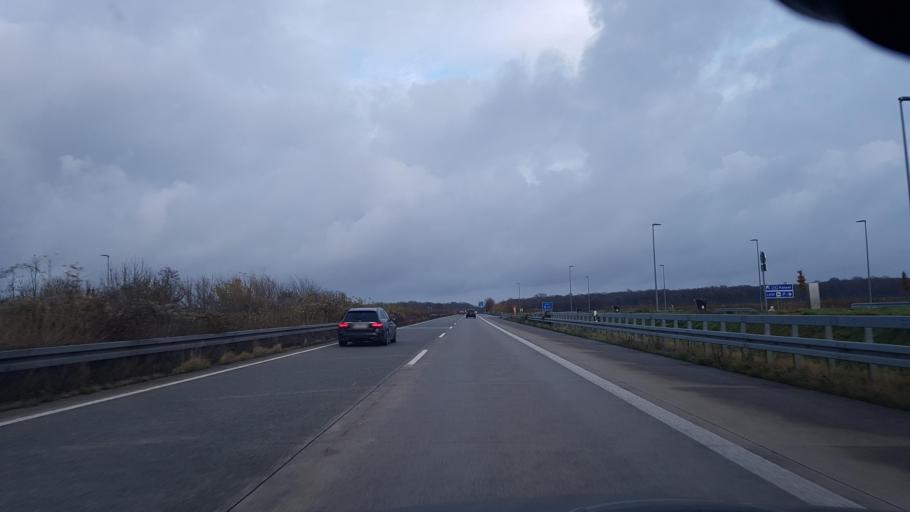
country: DE
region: North Rhine-Westphalia
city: Geseke
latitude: 51.5951
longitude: 8.4879
